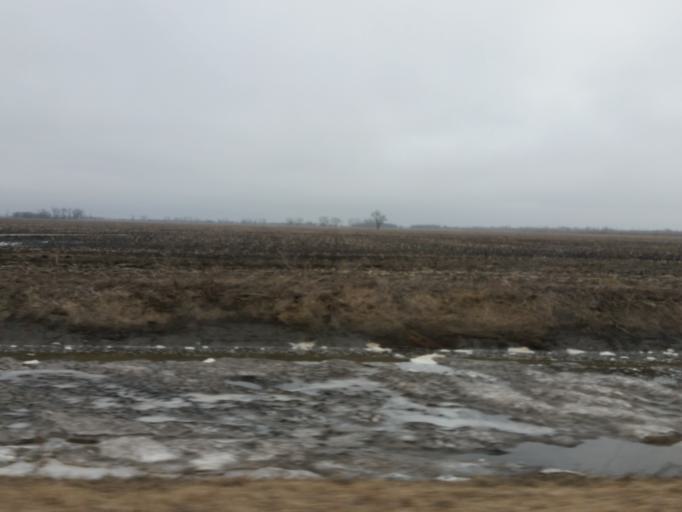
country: US
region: North Dakota
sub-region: Walsh County
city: Grafton
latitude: 48.3686
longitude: -97.1726
